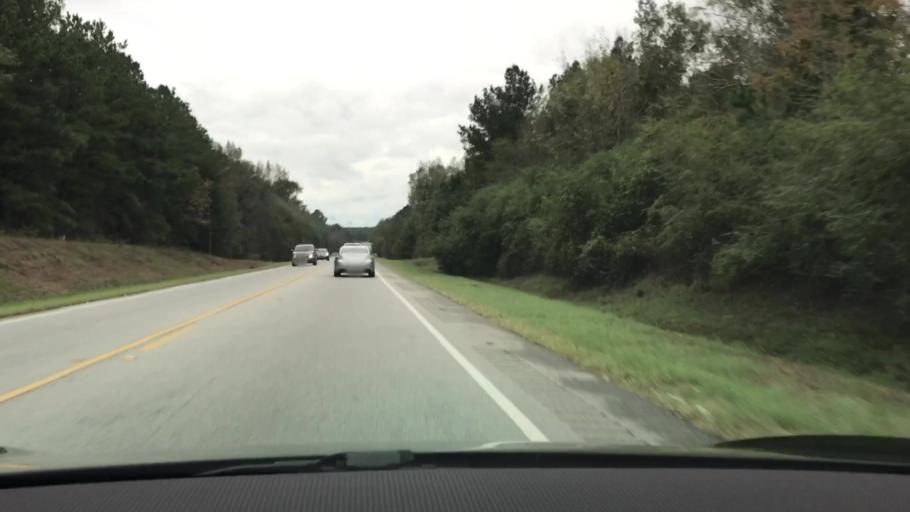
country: US
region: Georgia
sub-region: Jefferson County
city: Wadley
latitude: 32.9031
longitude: -82.3999
